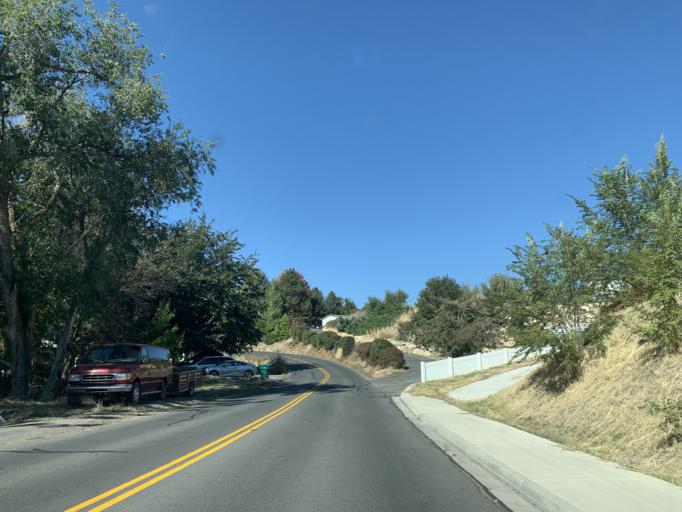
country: US
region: Utah
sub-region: Utah County
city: Orem
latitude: 40.2611
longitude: -111.6864
